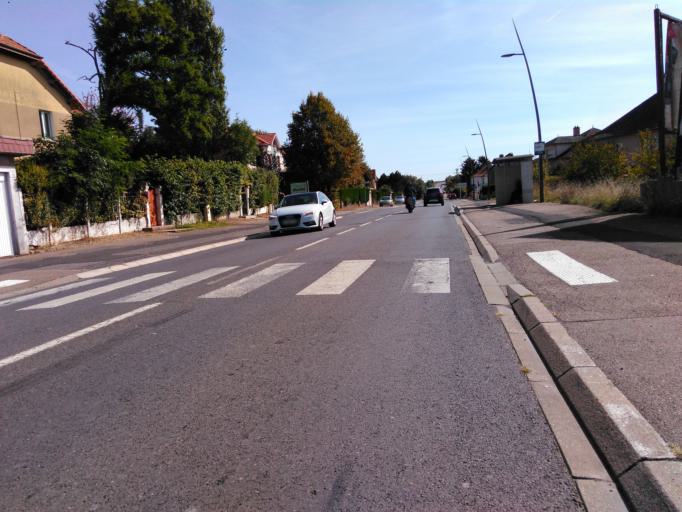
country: FR
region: Lorraine
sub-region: Departement de la Moselle
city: Hettange-Grande
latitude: 49.3993
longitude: 6.1612
